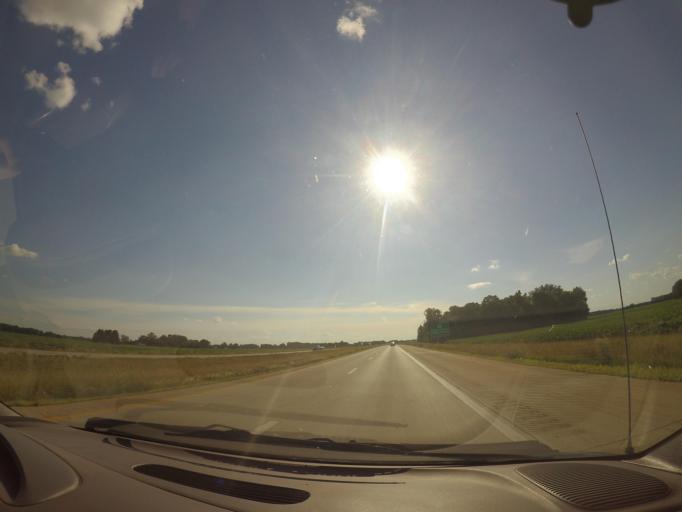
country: US
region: Ohio
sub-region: Lucas County
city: Whitehouse
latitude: 41.4561
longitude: -83.8075
